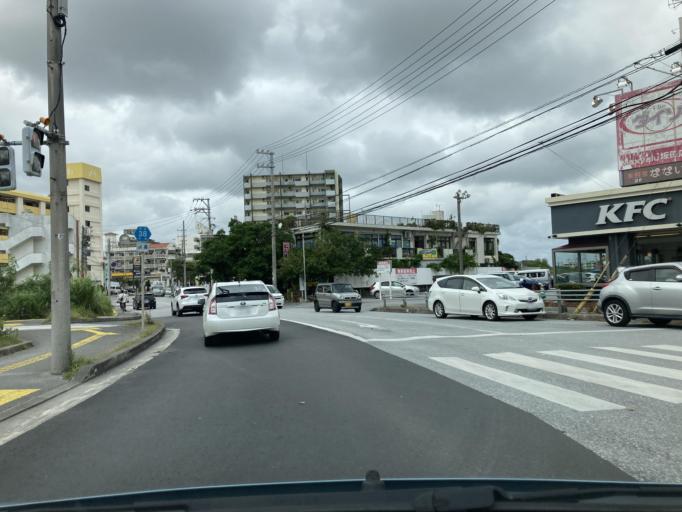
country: JP
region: Okinawa
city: Ginowan
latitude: 26.2387
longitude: 127.7489
